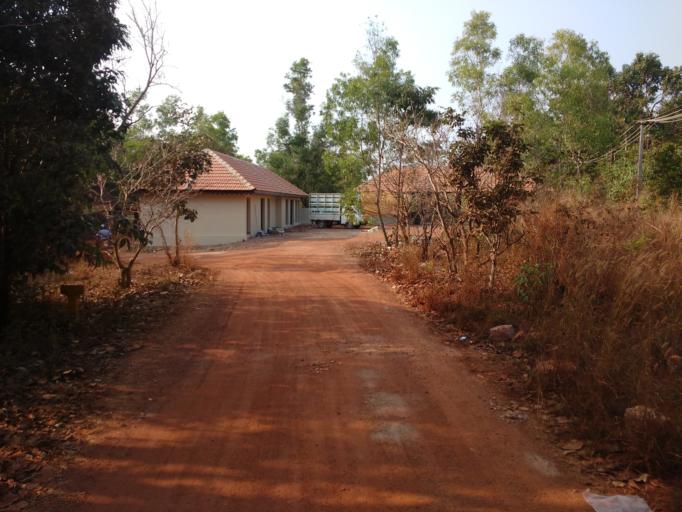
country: IN
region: Karnataka
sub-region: Dakshina Kannada
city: Mangalore
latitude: 12.9292
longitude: 74.9039
